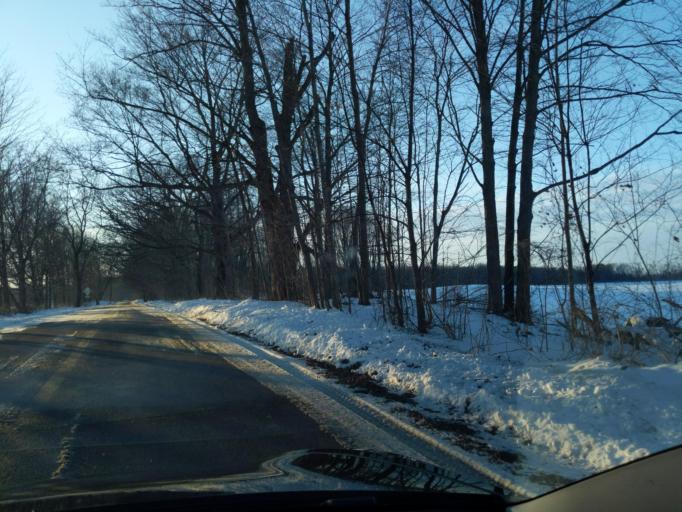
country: US
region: Michigan
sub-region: Ingham County
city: Webberville
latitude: 42.5682
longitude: -84.1440
